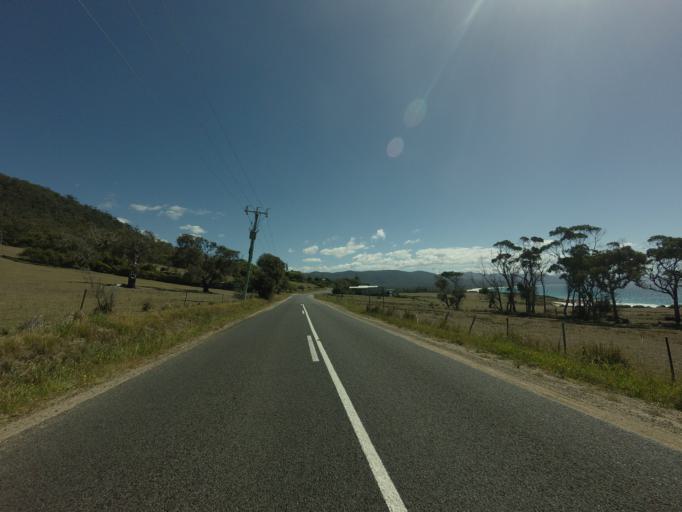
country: AU
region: Tasmania
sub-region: Break O'Day
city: St Helens
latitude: -41.8599
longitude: 148.2775
